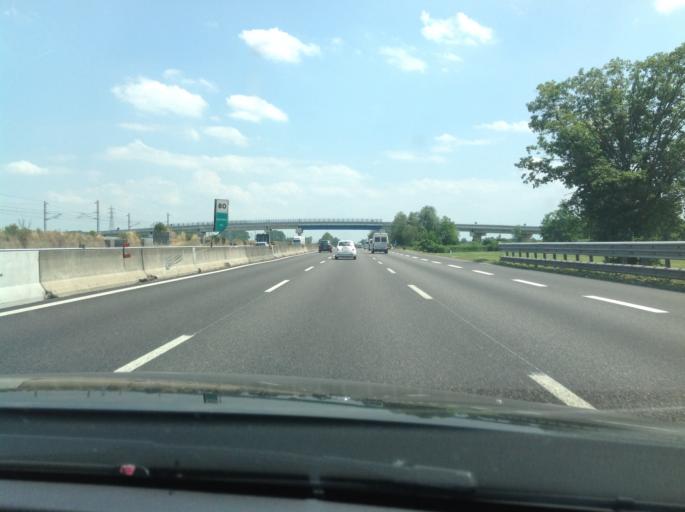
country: IT
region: Emilia-Romagna
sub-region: Provincia di Piacenza
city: Alseno
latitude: 44.9311
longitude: 9.9767
